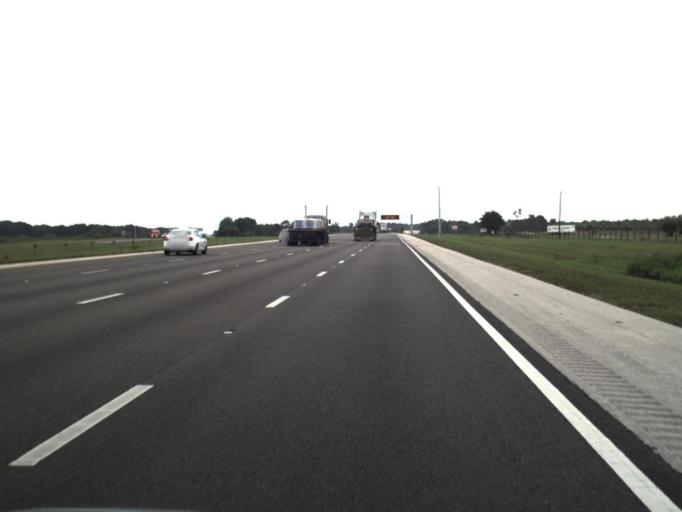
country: US
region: Florida
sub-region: Manatee County
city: Ellenton
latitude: 27.5724
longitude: -82.5149
